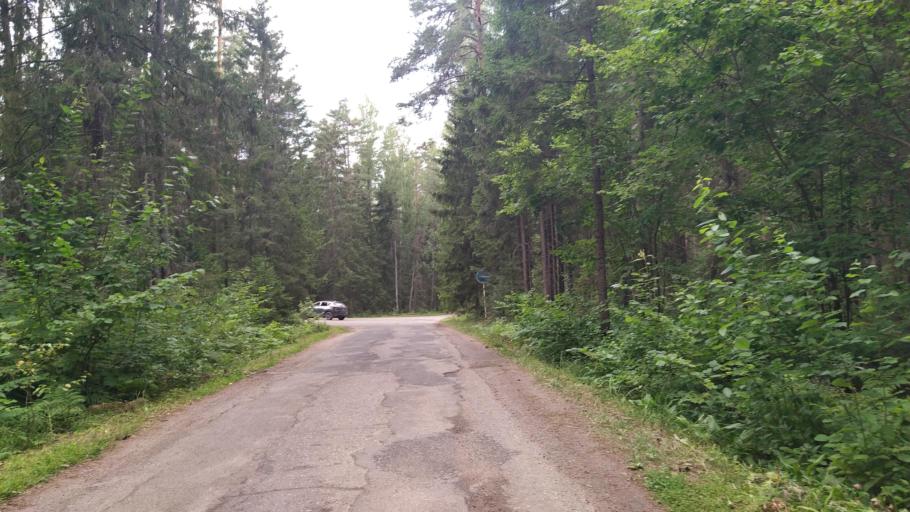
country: RU
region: Pskov
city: Pushkinskiye Gory
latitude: 57.0582
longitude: 28.9409
